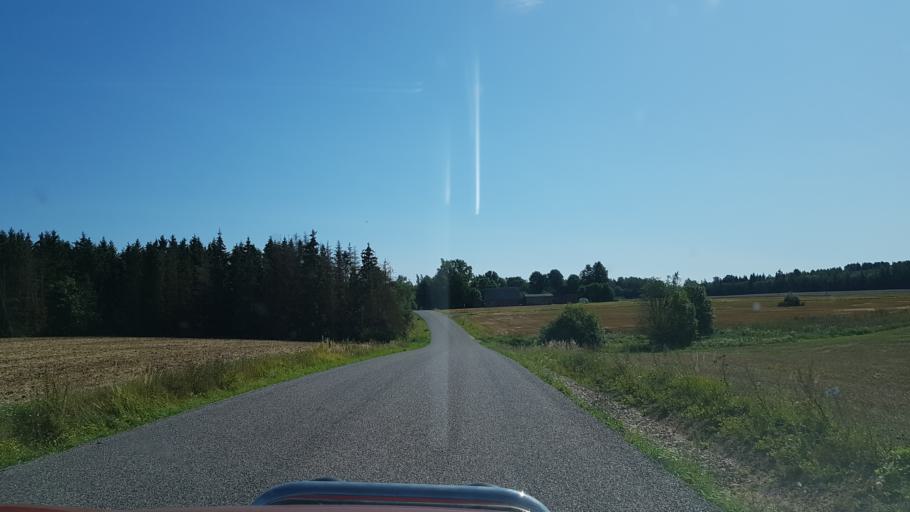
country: EE
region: Tartu
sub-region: Puhja vald
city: Puhja
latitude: 58.2581
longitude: 26.3156
